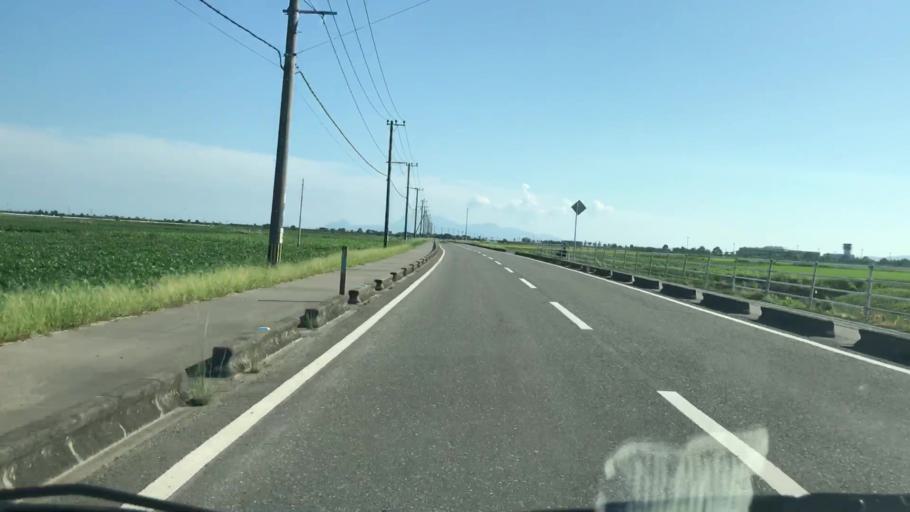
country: JP
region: Saga Prefecture
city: Okawa
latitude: 33.1645
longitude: 130.3089
